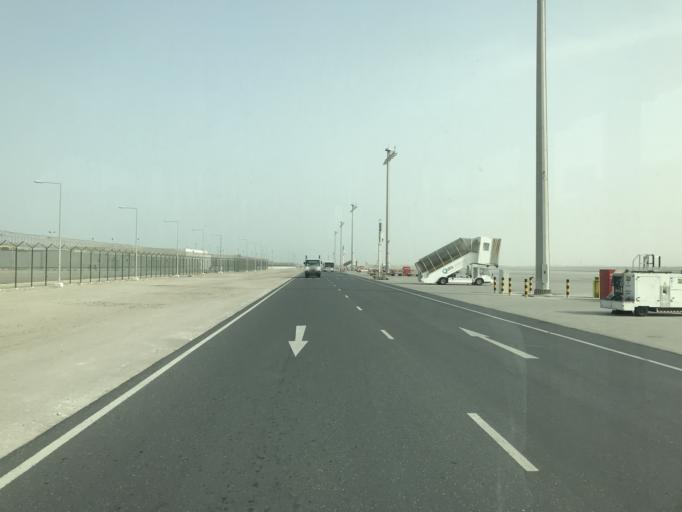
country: QA
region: Baladiyat ad Dawhah
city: Doha
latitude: 25.2749
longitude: 51.6007
